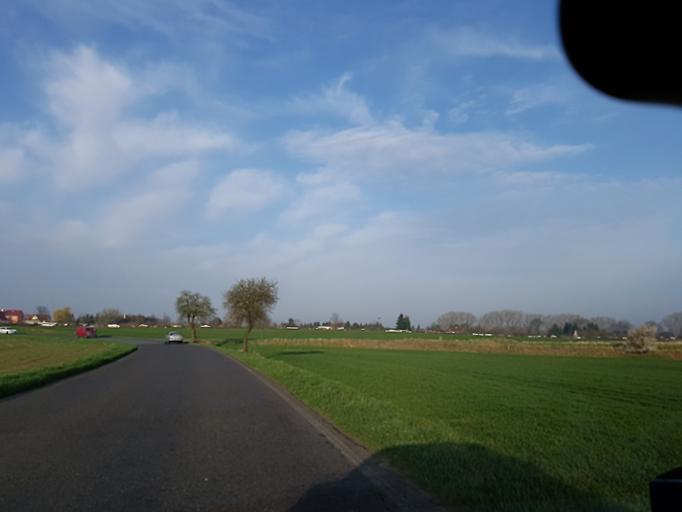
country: DE
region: Saxony
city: Riesa
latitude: 51.3285
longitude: 13.3023
